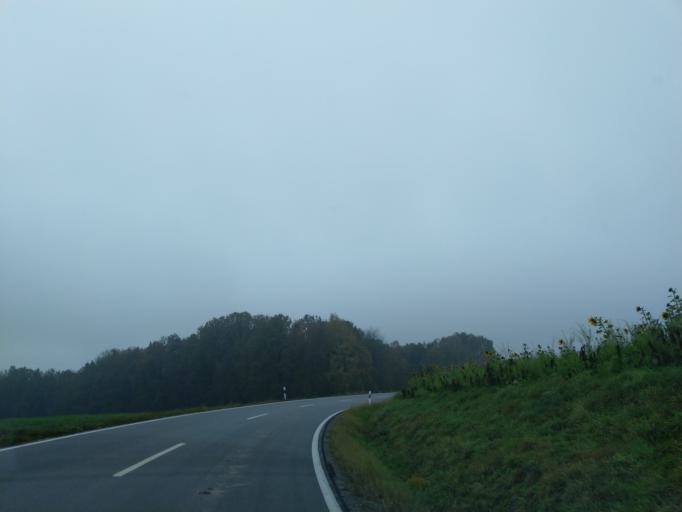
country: DE
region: Bavaria
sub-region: Lower Bavaria
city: Grattersdorf
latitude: 48.7898
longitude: 13.1458
